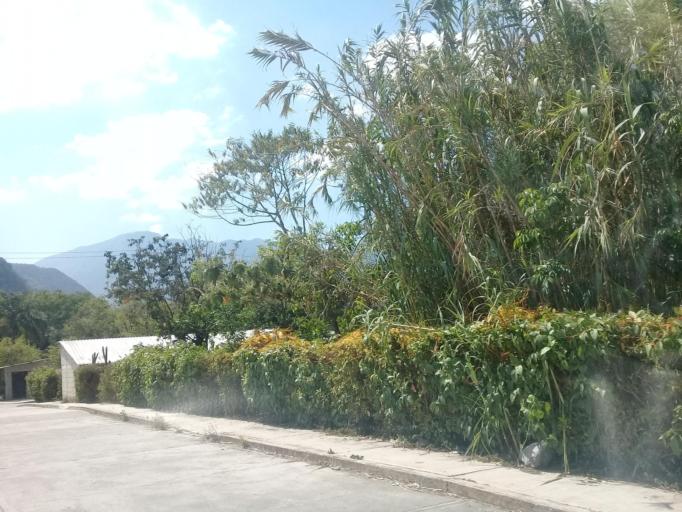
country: MX
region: Veracruz
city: Jalapilla
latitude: 18.8048
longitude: -97.0717
